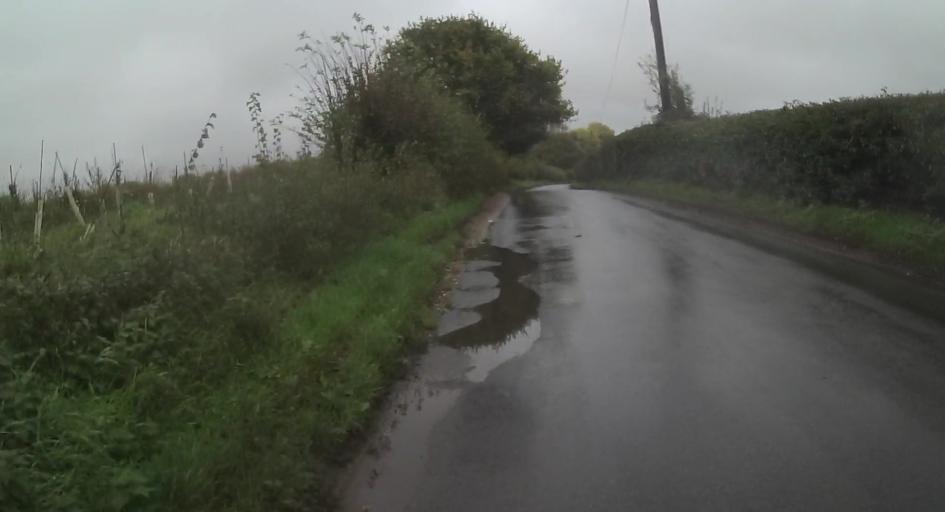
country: GB
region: England
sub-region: Surrey
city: Farnham
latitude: 51.2146
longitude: -0.8503
